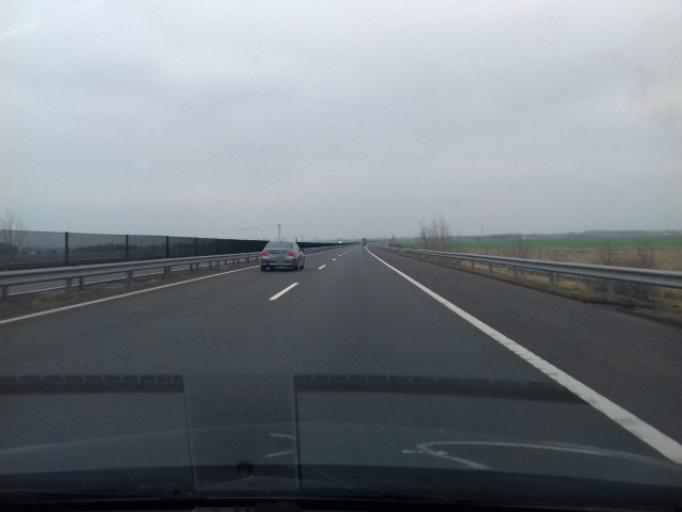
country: HU
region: Hajdu-Bihar
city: Hajdunanas
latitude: 47.8467
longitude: 21.3450
